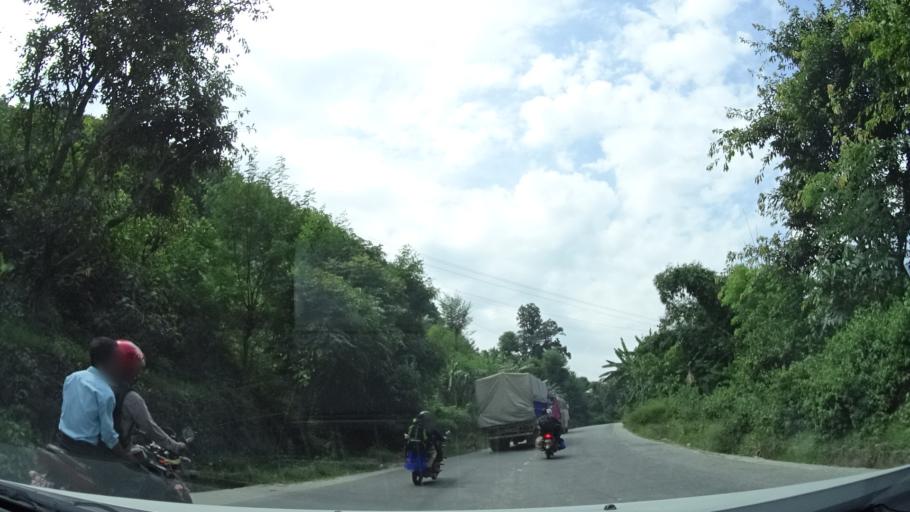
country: NP
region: Central Region
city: Kirtipur
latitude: 27.8093
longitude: 84.9664
